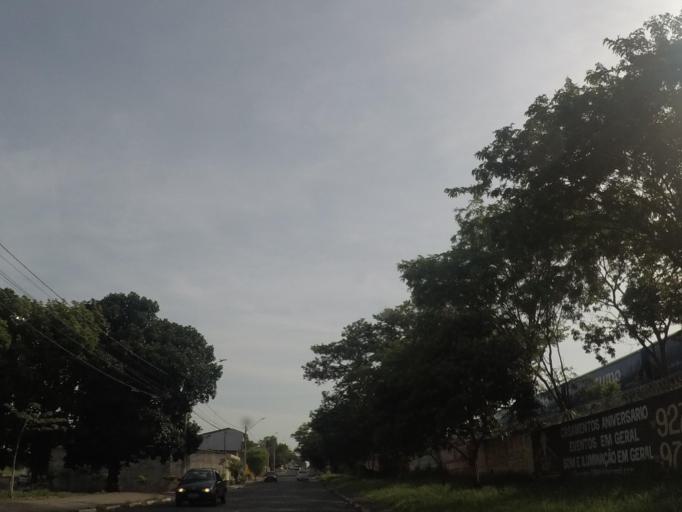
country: BR
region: Sao Paulo
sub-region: Hortolandia
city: Hortolandia
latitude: -22.8578
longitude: -47.1962
